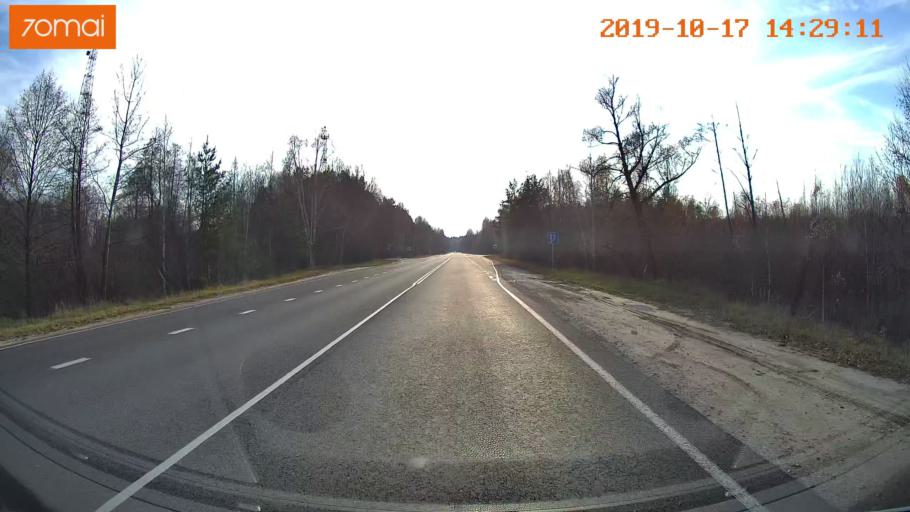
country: RU
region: Rjazan
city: Solotcha
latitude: 54.9639
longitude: 39.9449
